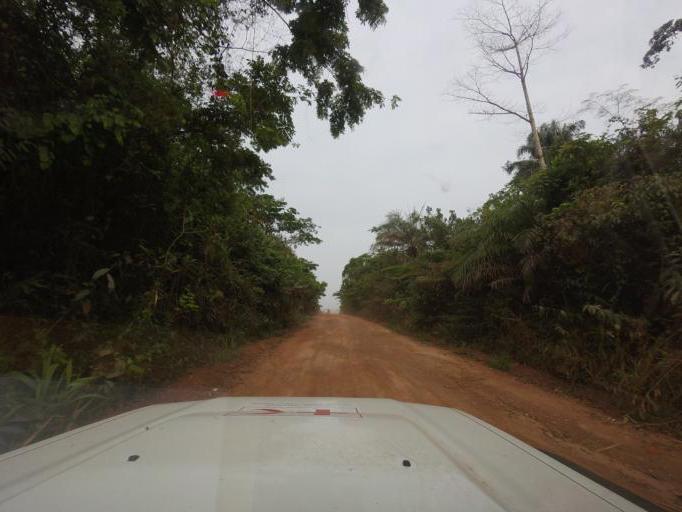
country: LR
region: Lofa
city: Voinjama
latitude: 8.3757
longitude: -9.8764
